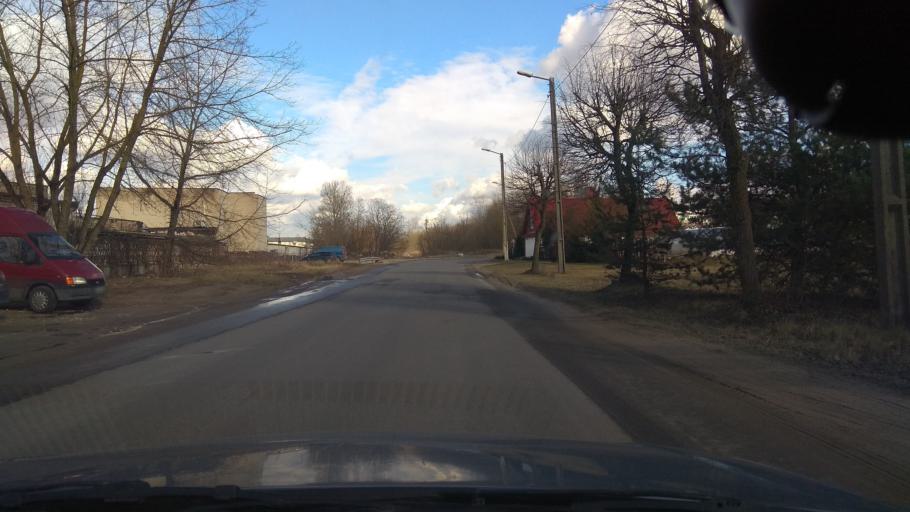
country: LT
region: Vilnius County
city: Lazdynai
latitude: 54.6457
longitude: 25.2170
